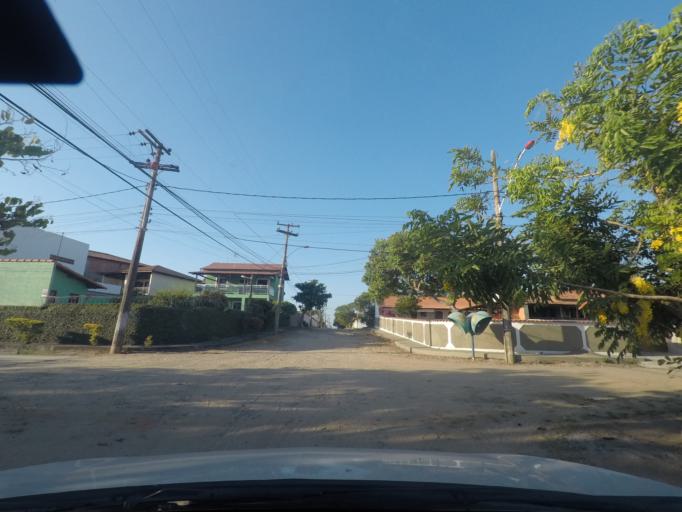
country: BR
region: Rio de Janeiro
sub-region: Marica
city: Marica
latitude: -22.9696
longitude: -42.9316
